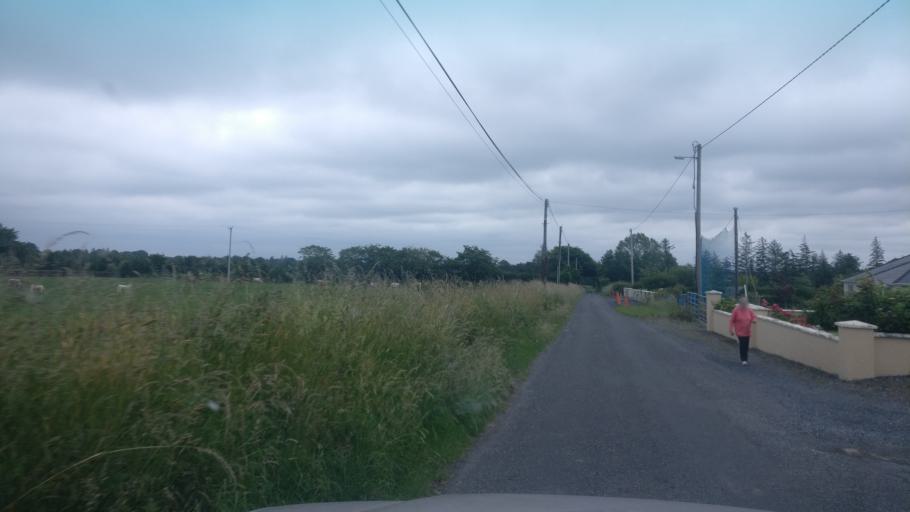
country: IE
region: Connaught
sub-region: County Galway
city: Ballinasloe
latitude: 53.3052
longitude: -8.3576
